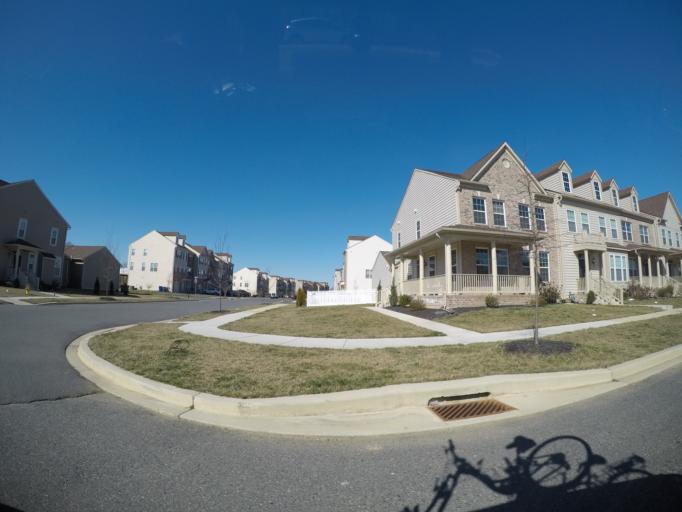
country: US
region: Delaware
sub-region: New Castle County
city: Middletown
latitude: 39.5144
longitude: -75.6712
